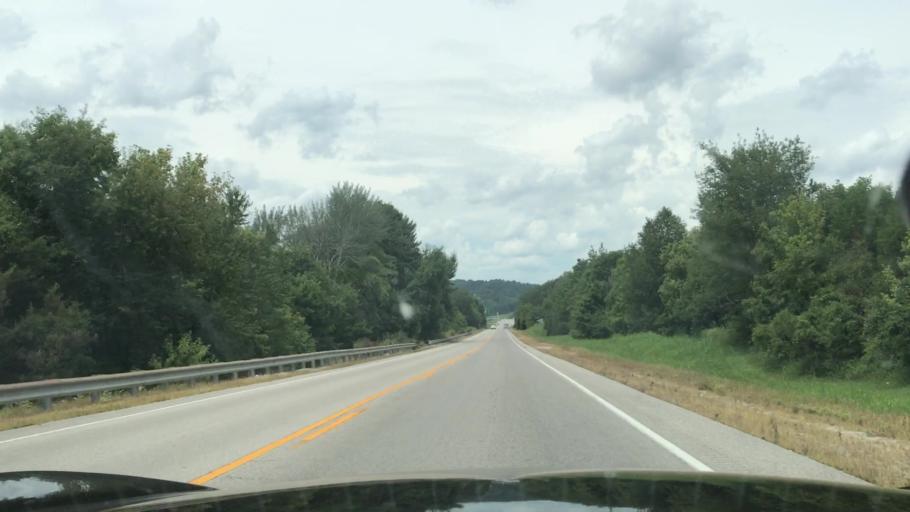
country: US
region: Kentucky
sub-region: Hart County
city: Horse Cave
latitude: 37.1949
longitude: -85.9264
